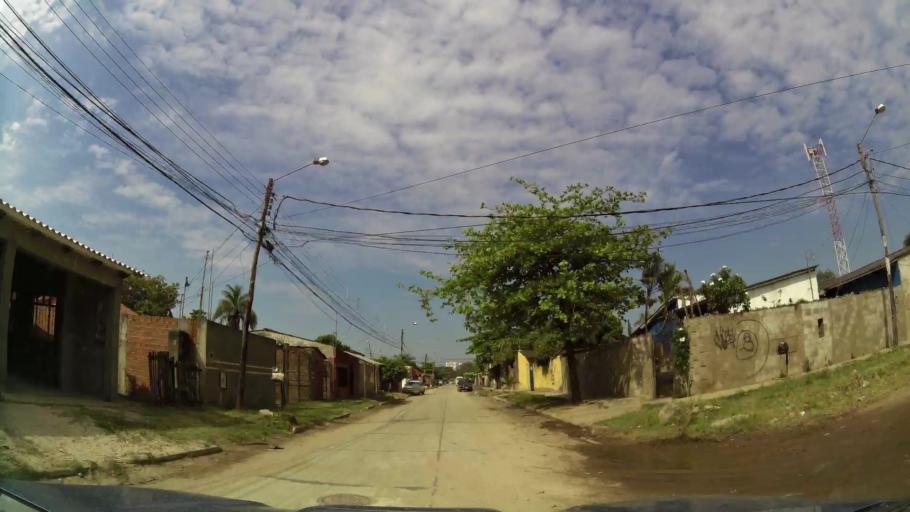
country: BO
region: Santa Cruz
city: Santa Cruz de la Sierra
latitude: -17.7276
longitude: -63.1805
